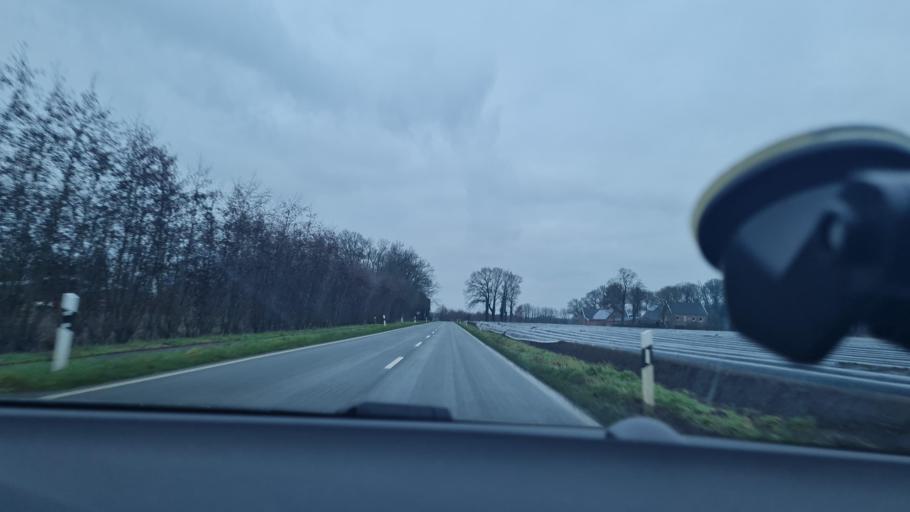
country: DE
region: North Rhine-Westphalia
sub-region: Regierungsbezirk Munster
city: Heiden
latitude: 51.7812
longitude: 6.9154
